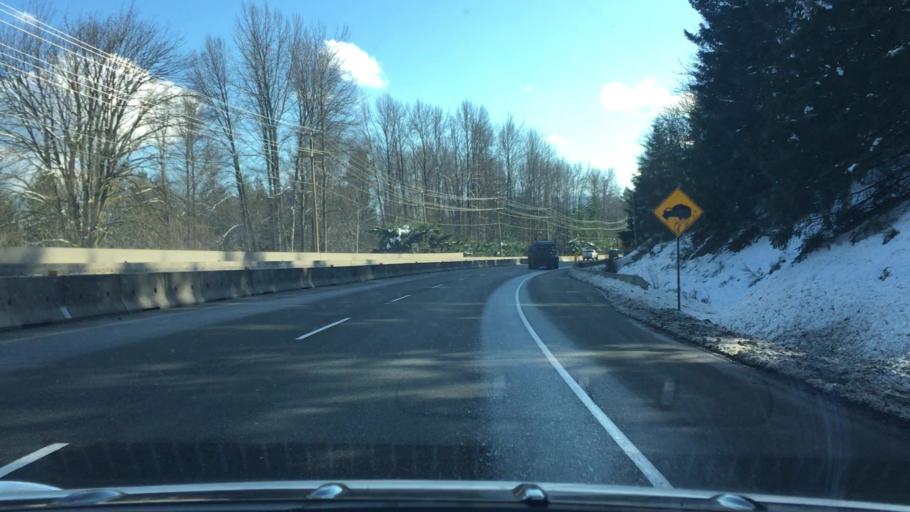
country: CA
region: British Columbia
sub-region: Cowichan Valley Regional District
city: Ladysmith
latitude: 49.0656
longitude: -123.8772
